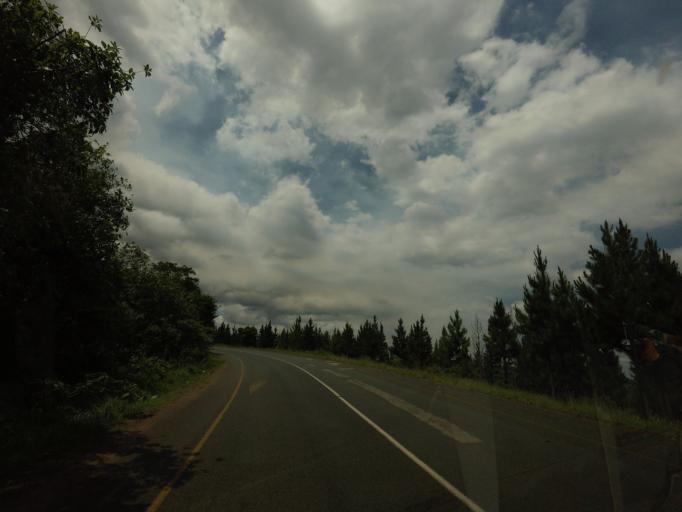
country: ZA
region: Mpumalanga
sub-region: Ehlanzeni District
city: Graksop
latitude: -24.9363
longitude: 30.8129
